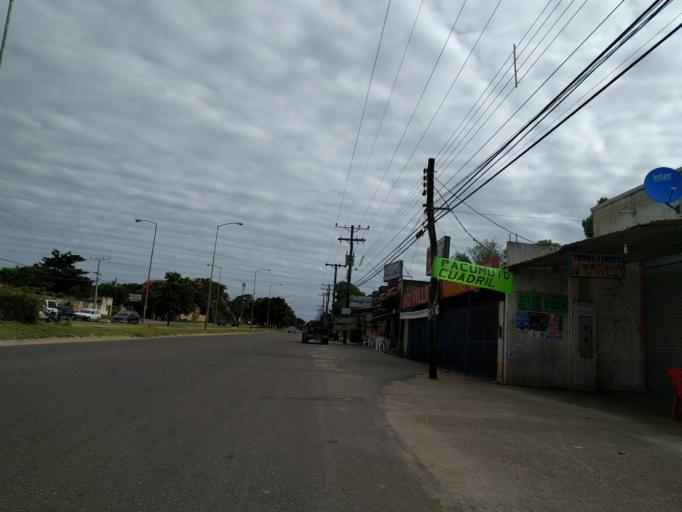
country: BO
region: Santa Cruz
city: Santa Cruz de la Sierra
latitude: -17.8389
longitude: -63.2391
